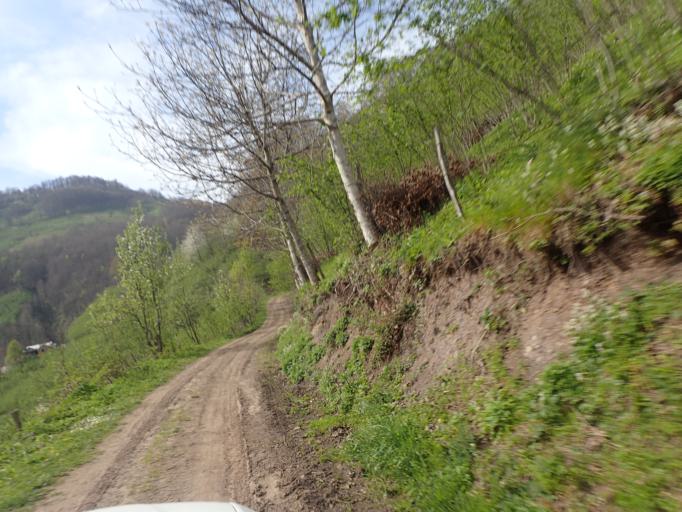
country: TR
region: Ordu
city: Aybasti
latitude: 40.7196
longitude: 37.2996
